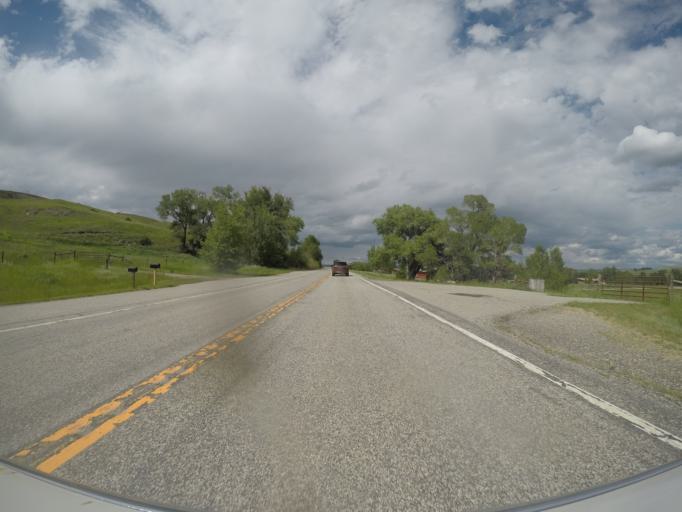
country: US
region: Montana
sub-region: Sweet Grass County
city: Big Timber
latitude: 45.8117
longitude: -109.9595
